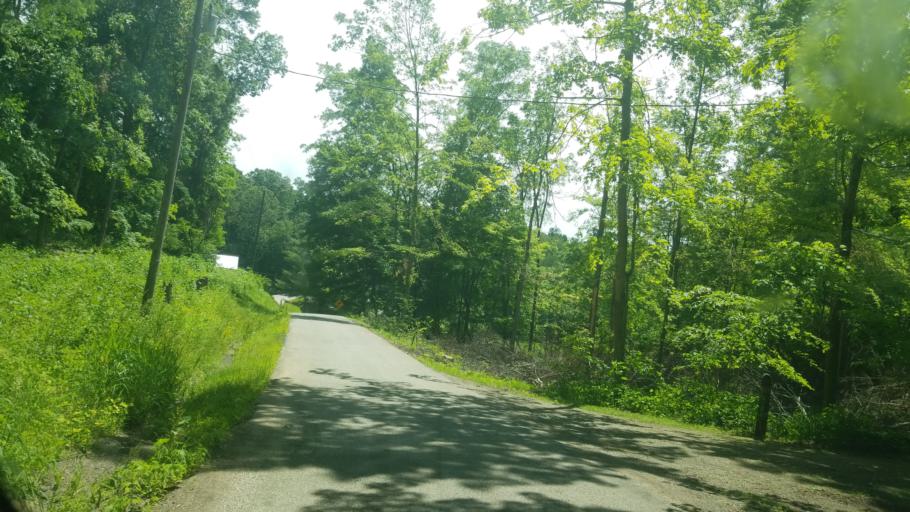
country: US
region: Ohio
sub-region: Sandusky County
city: Bellville
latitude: 40.6166
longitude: -82.4630
